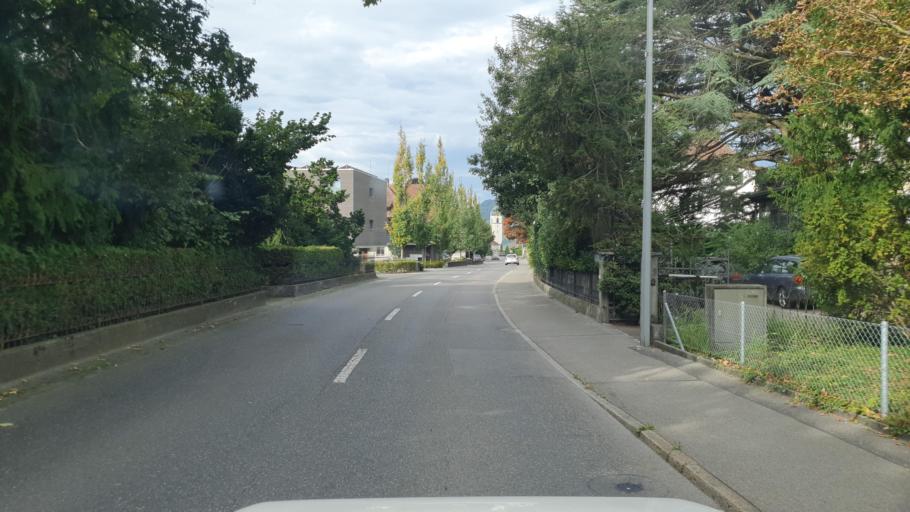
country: CH
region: Aargau
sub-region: Bezirk Lenzburg
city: Meisterschwanden
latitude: 47.2950
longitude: 8.2404
